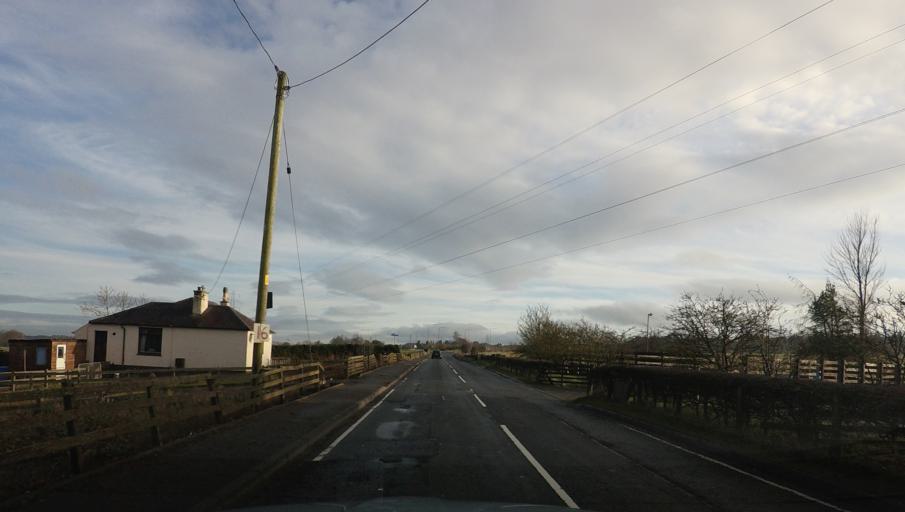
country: GB
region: Scotland
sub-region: West Lothian
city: East Calder
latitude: 55.8903
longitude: -3.4508
